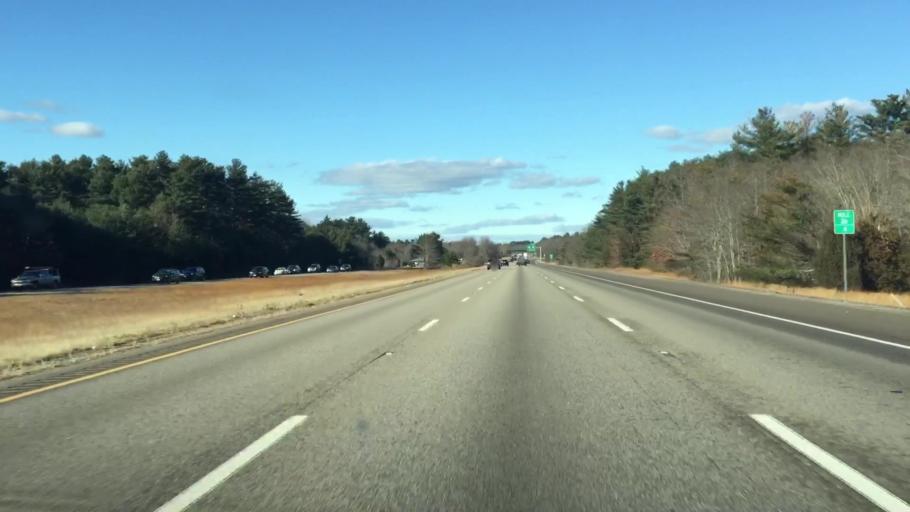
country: US
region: Massachusetts
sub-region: Bristol County
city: Norton Center
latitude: 41.9761
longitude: -71.1521
